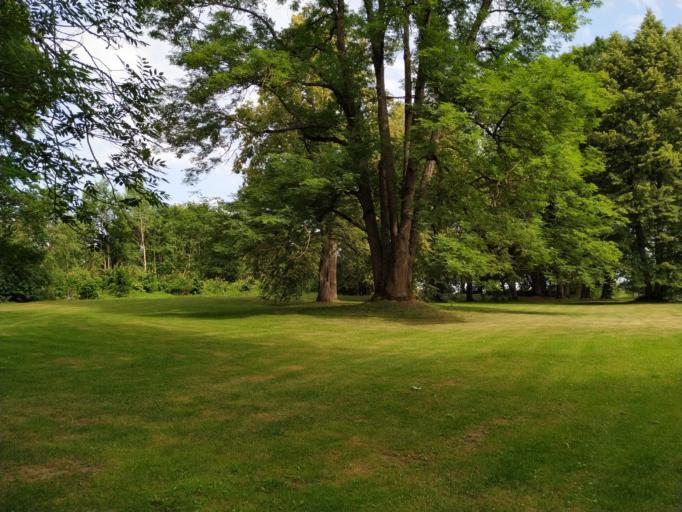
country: LT
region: Panevezys
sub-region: Birzai
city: Birzai
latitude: 56.2154
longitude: 24.6822
